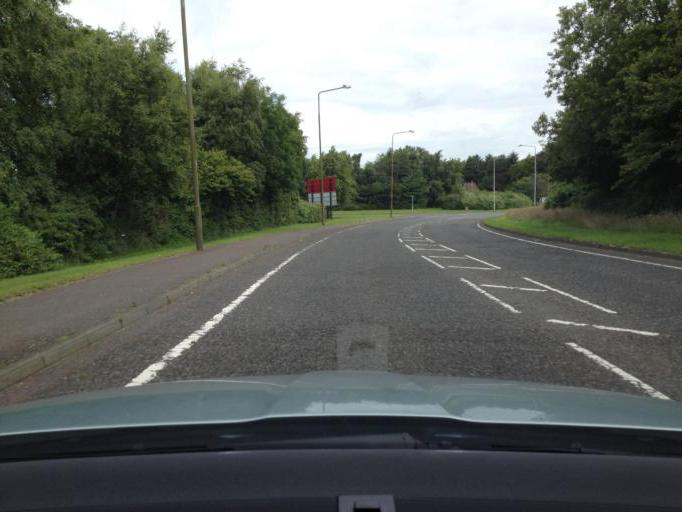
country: GB
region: Scotland
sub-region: West Lothian
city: Livingston
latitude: 55.8757
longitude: -3.5423
